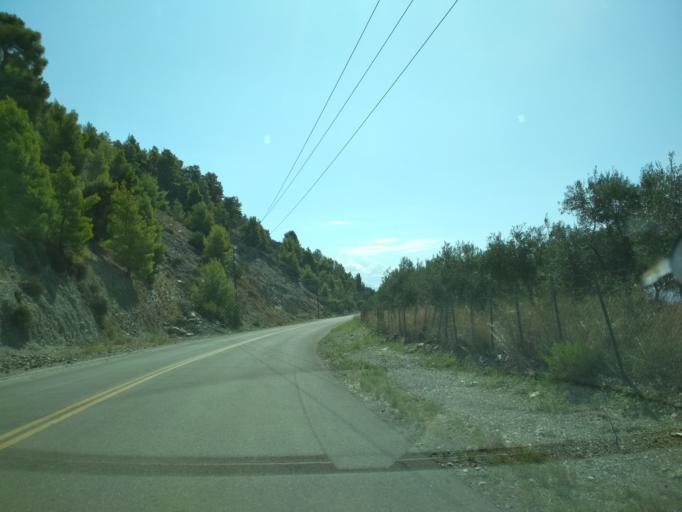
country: GR
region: Central Greece
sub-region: Nomos Evvoias
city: Roviai
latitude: 38.8349
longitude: 23.1961
